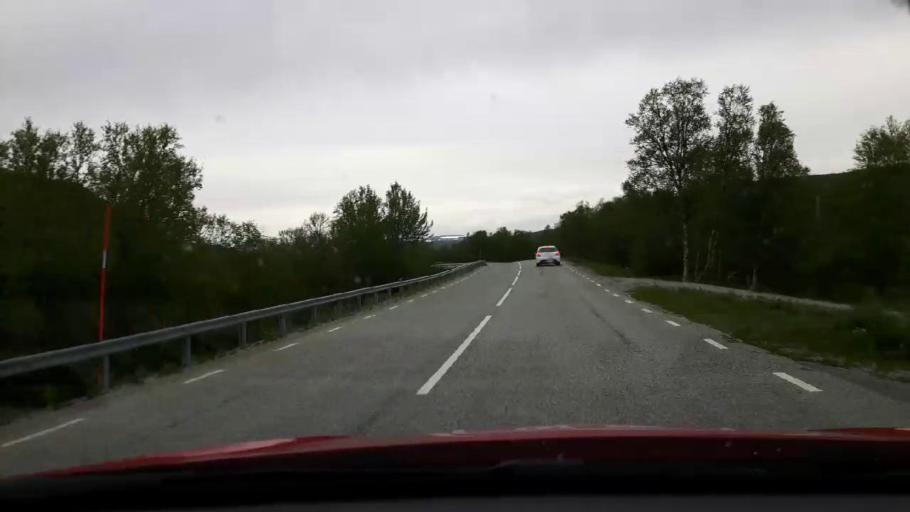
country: NO
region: Sor-Trondelag
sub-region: Tydal
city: Aas
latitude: 62.6808
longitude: 12.4174
